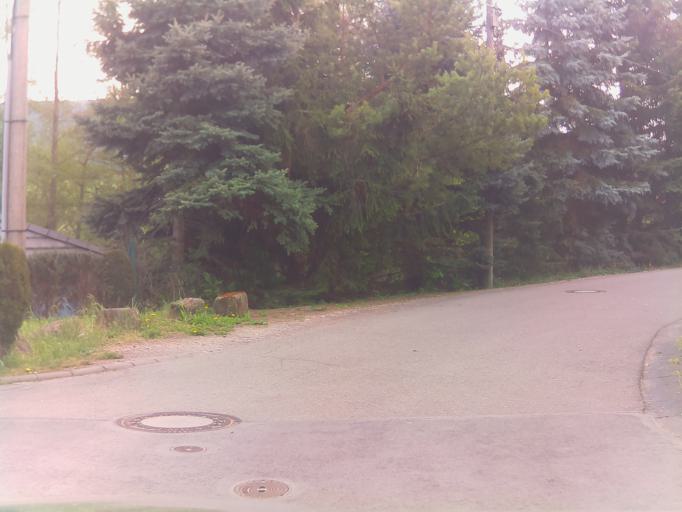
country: DE
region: Thuringia
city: Plaue
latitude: 50.7984
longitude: 10.9165
